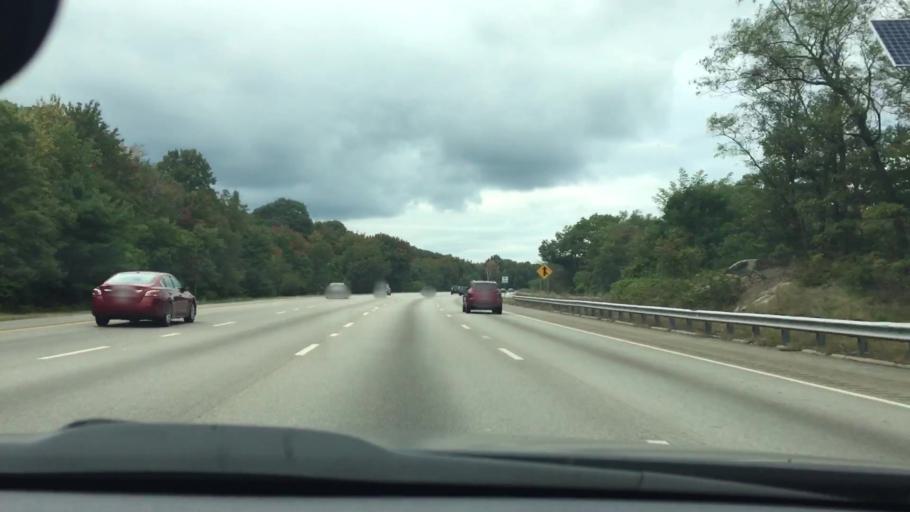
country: US
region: Massachusetts
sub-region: Norfolk County
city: Westwood
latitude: 42.2468
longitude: -71.2046
